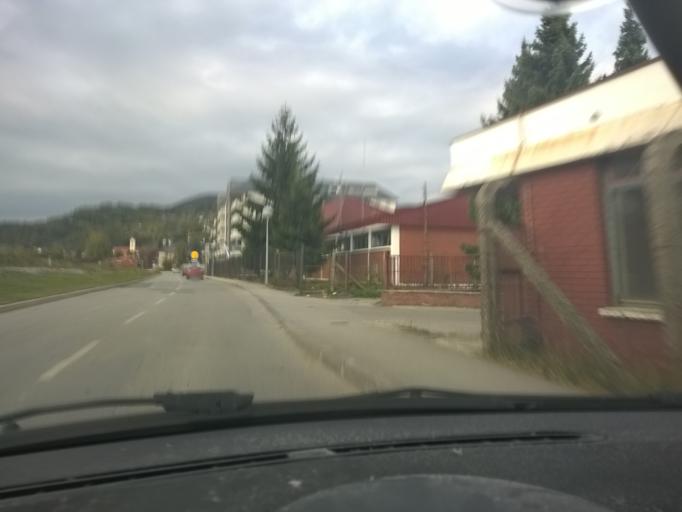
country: HR
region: Krapinsko-Zagorska
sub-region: Grad Krapina
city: Krapina
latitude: 46.1553
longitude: 15.8739
